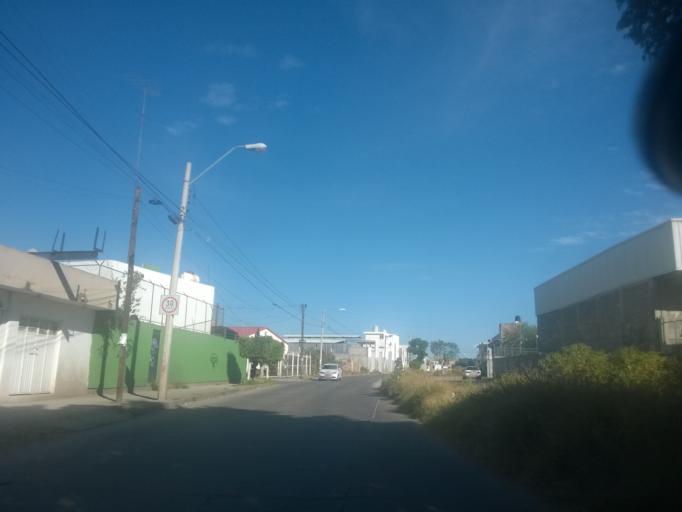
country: MX
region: Guanajuato
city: Leon
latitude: 21.1251
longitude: -101.6508
